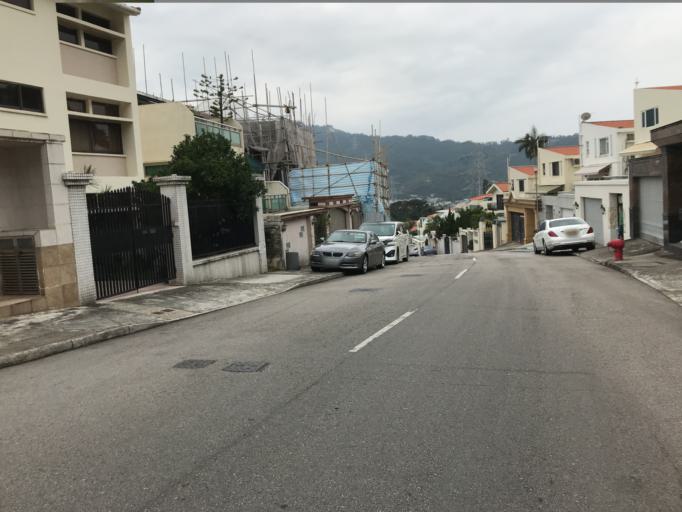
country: HK
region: Tai Po
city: Tai Po
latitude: 22.4650
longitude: 114.1582
